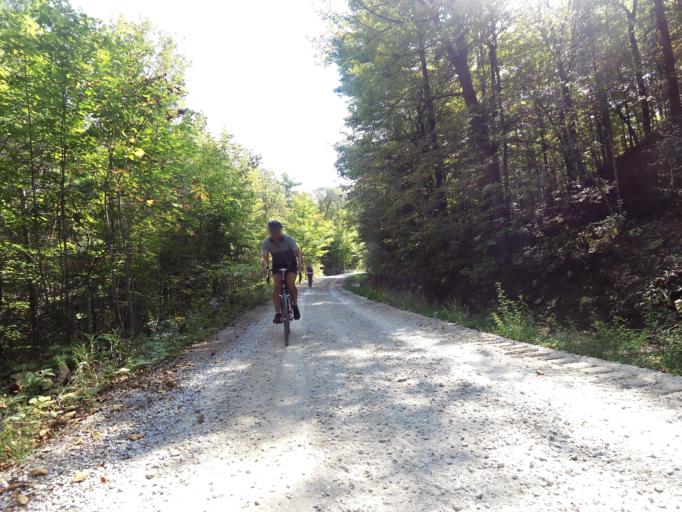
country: CA
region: Ontario
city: Perth
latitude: 45.0180
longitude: -76.6015
